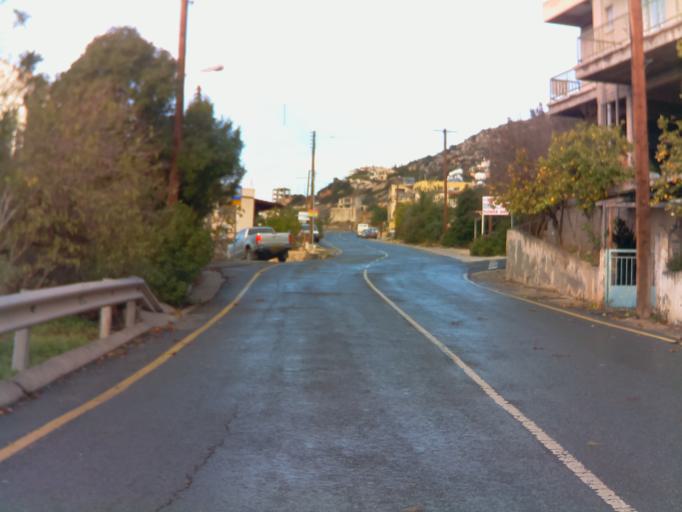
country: CY
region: Pafos
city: Pegeia
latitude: 34.8848
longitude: 32.3794
